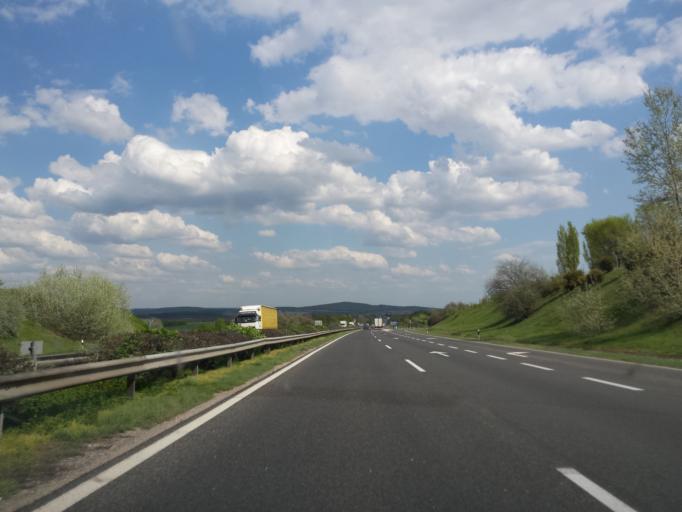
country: HU
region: Pest
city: Zsambek
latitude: 47.5089
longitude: 18.7522
